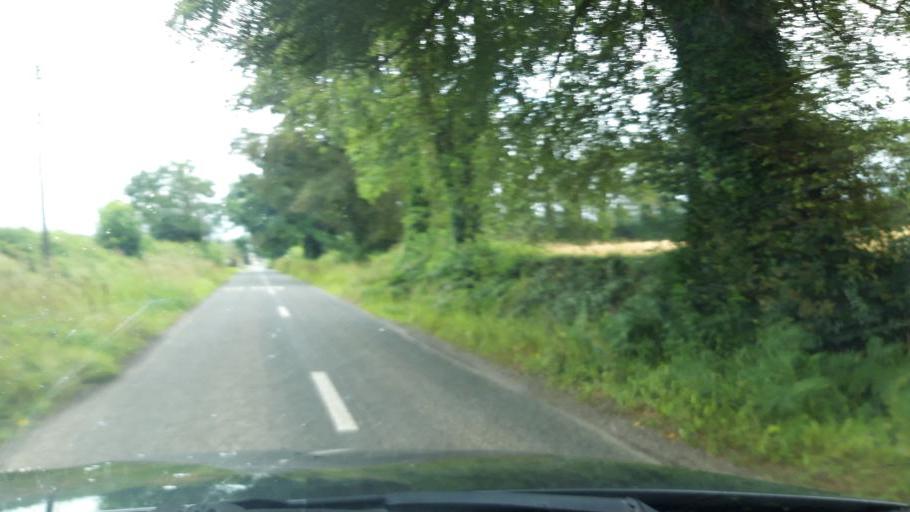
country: IE
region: Munster
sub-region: County Cork
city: Castlemartyr
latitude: 52.1354
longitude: -8.0250
